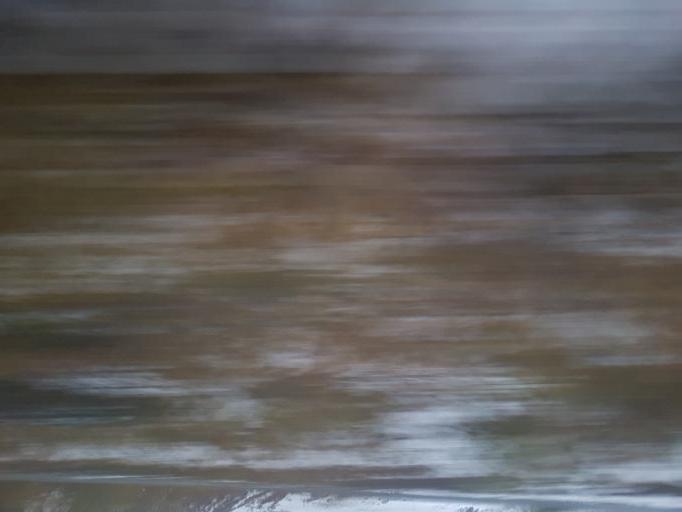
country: NO
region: Sor-Trondelag
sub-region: Oppdal
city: Oppdal
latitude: 62.5302
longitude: 9.6160
